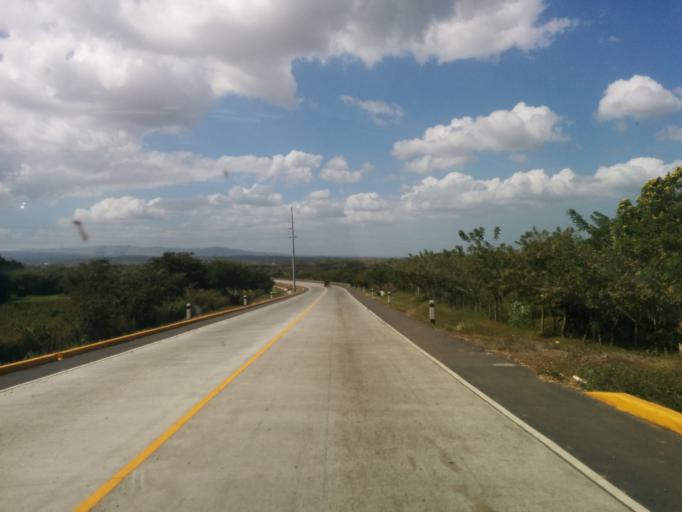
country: NI
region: Masaya
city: Masaya
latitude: 12.0023
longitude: -86.0914
